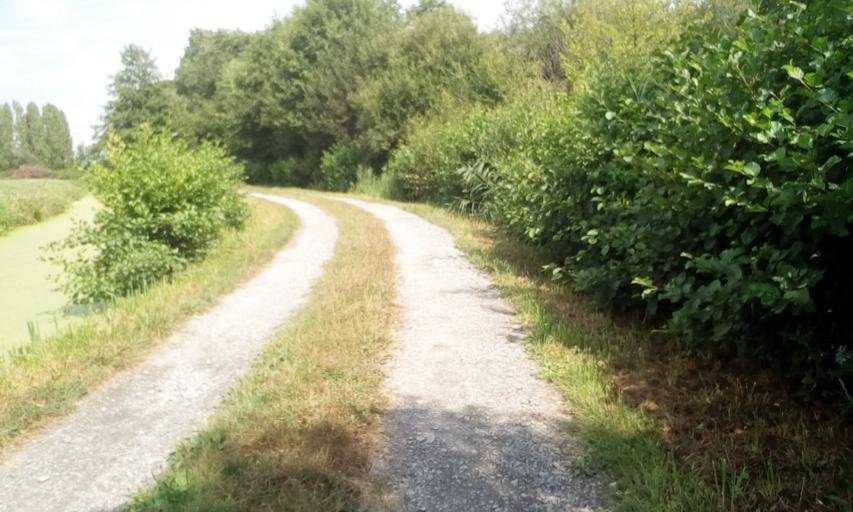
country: FR
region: Lower Normandy
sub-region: Departement du Calvados
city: Bavent
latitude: 49.2400
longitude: -0.1699
